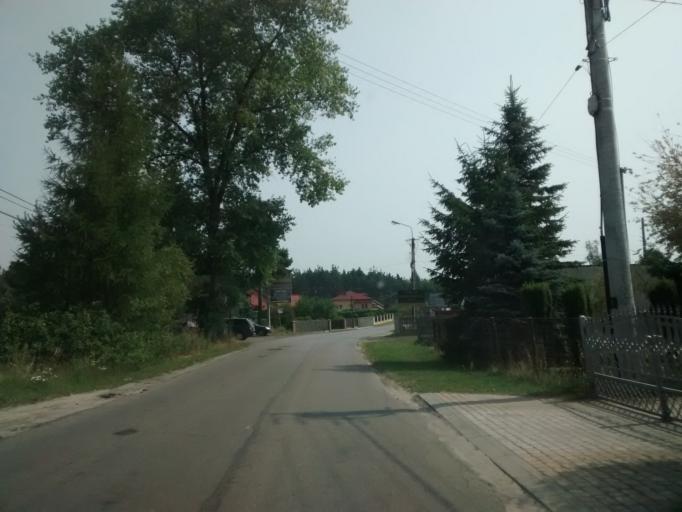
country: PL
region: Lesser Poland Voivodeship
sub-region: Powiat olkuski
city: Klucze
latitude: 50.3650
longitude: 19.5444
